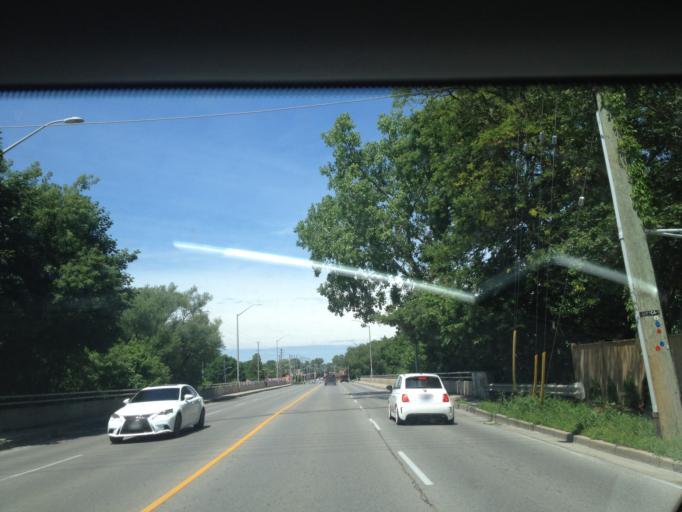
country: CA
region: Ontario
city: London
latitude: 42.9797
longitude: -81.2624
